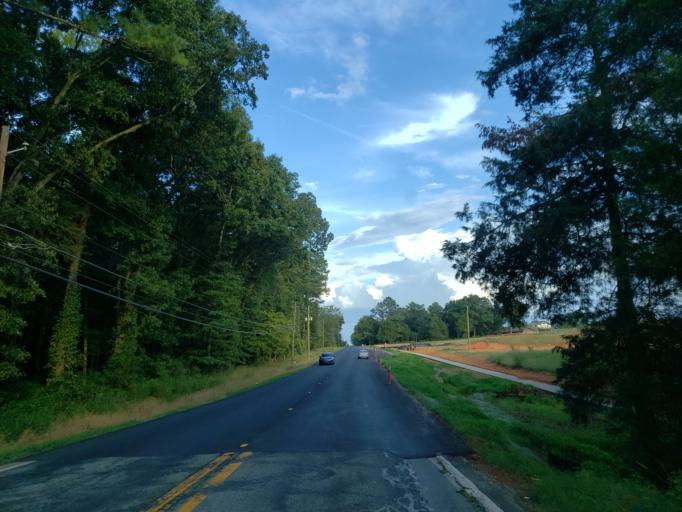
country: US
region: Georgia
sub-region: Bartow County
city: Cartersville
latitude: 34.2385
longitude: -84.8756
